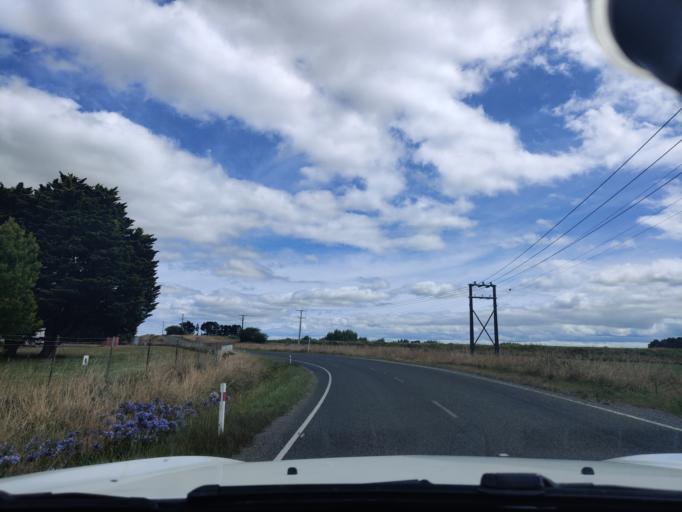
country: NZ
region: Manawatu-Wanganui
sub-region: Horowhenua District
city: Foxton
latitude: -40.5297
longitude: 175.4038
